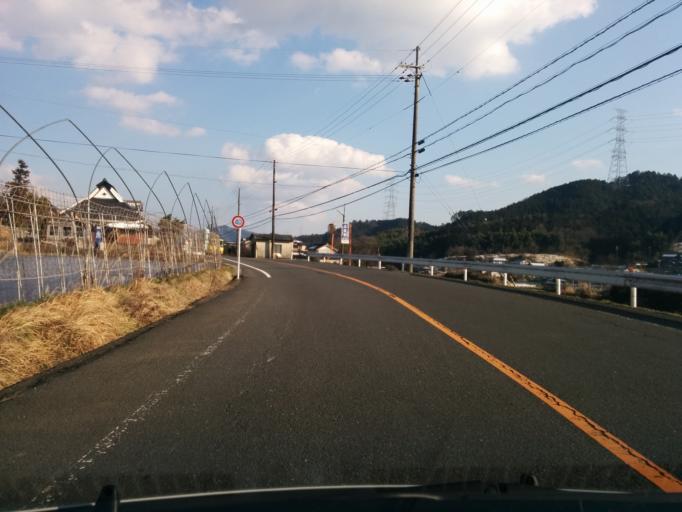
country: JP
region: Kyoto
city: Ayabe
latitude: 35.3654
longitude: 135.2003
